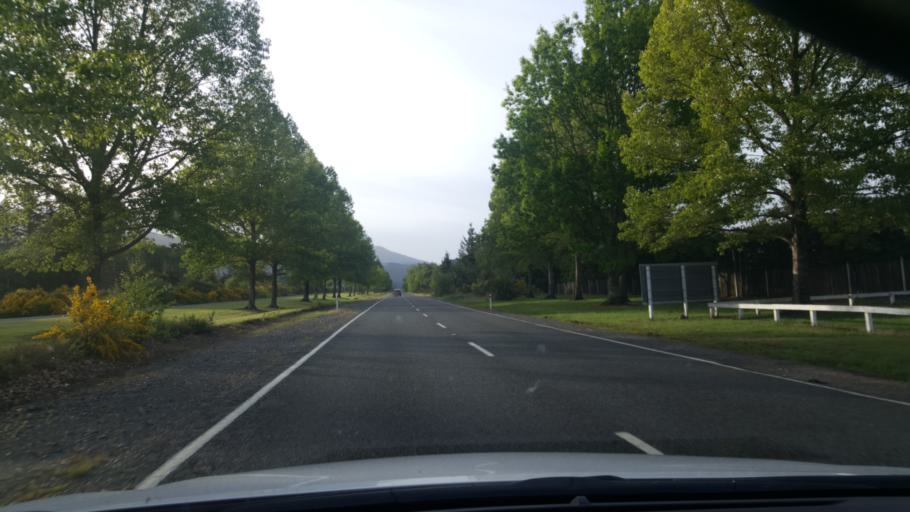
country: NZ
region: Waikato
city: Turangi
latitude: -38.9944
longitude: 175.8002
